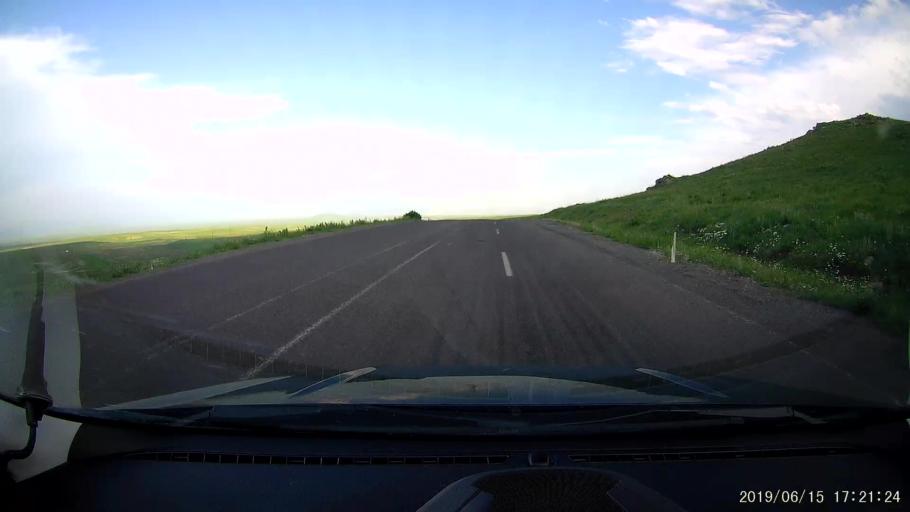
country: TR
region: Kars
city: Basgedikler
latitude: 40.6175
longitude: 43.3242
